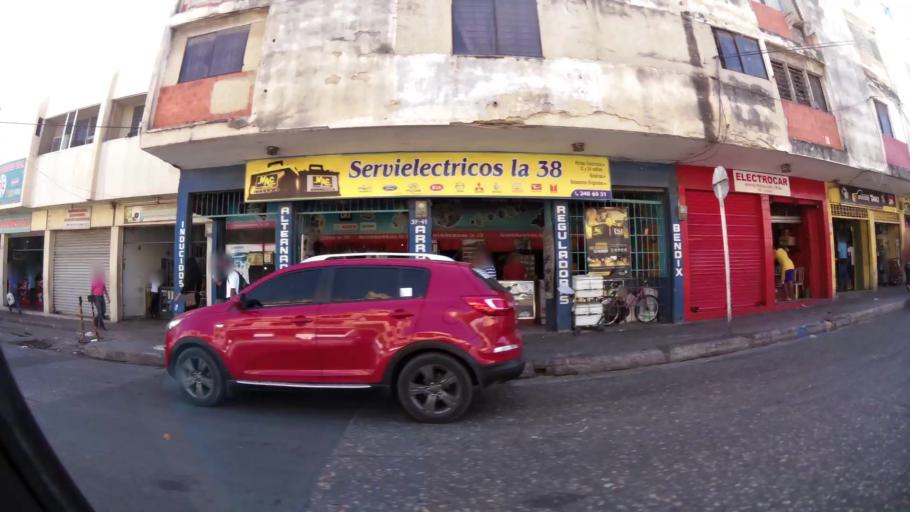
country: CO
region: Atlantico
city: Barranquilla
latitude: 10.9780
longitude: -74.7815
